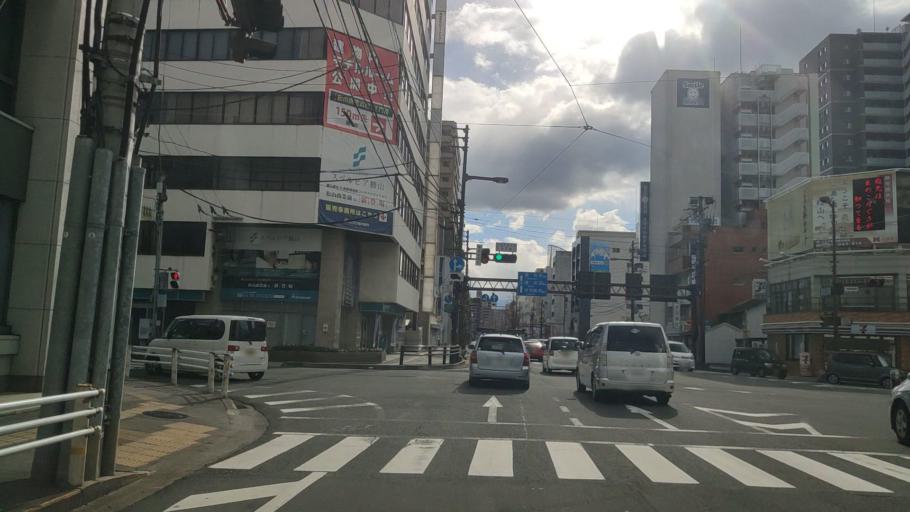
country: JP
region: Ehime
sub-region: Shikoku-chuo Shi
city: Matsuyama
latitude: 33.8419
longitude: 132.7755
